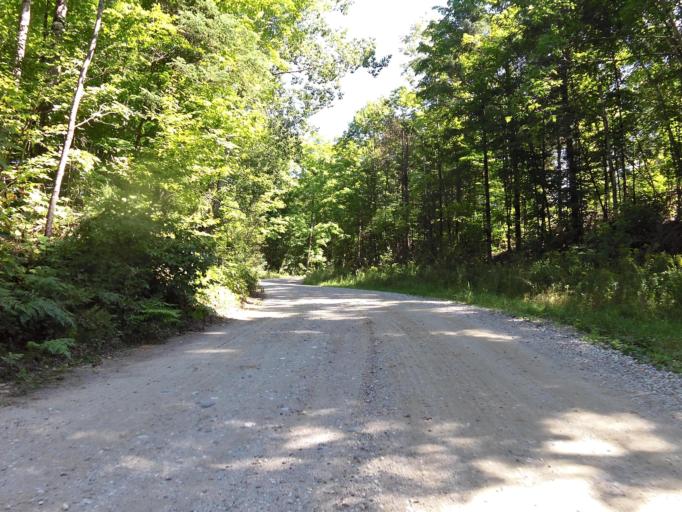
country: CA
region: Ontario
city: Renfrew
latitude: 45.1320
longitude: -76.6968
